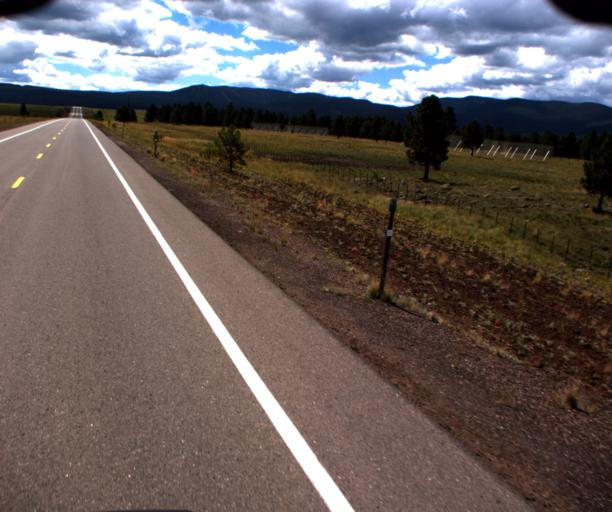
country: US
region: Arizona
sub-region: Apache County
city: Eagar
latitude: 34.0337
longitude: -109.5863
